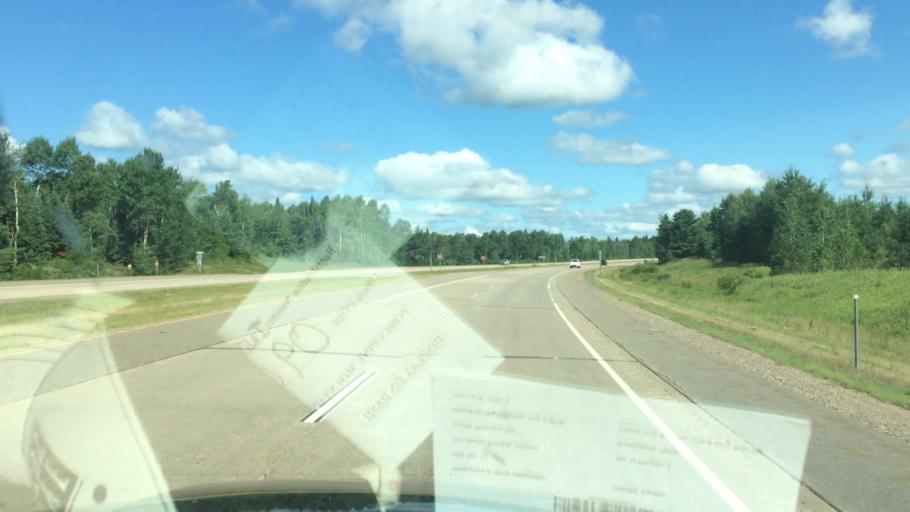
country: US
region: Wisconsin
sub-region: Lincoln County
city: Tomahawk
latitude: 45.3800
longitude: -89.6704
